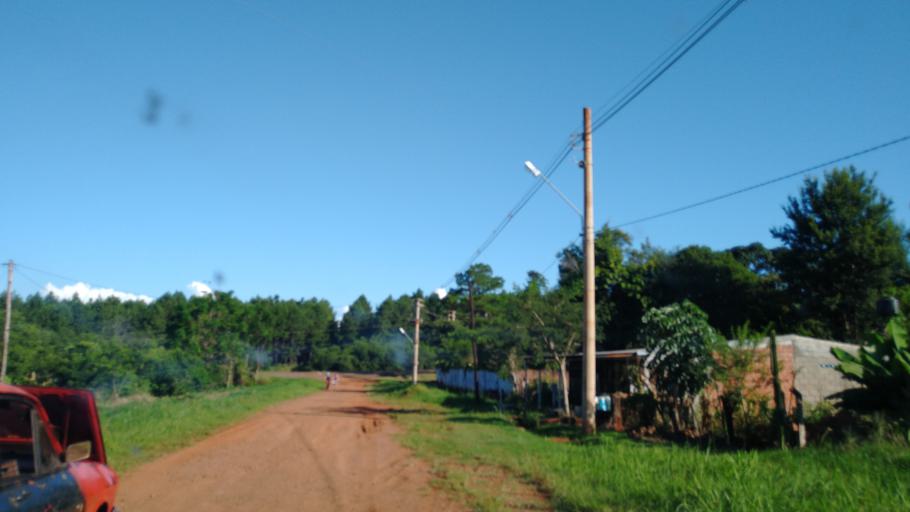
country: AR
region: Misiones
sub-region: Departamento de San Ignacio
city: San Ignacio
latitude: -27.2537
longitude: -55.5255
